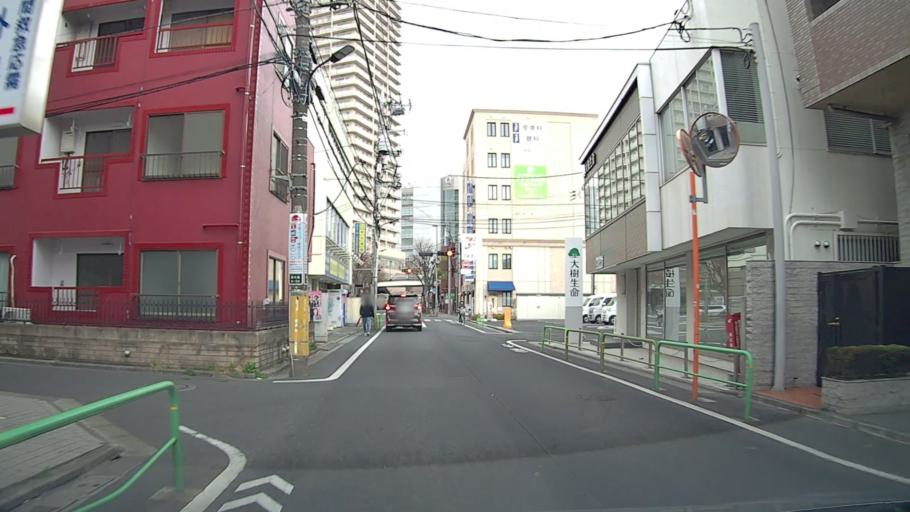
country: JP
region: Tokyo
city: Musashino
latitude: 35.7479
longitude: 139.5861
